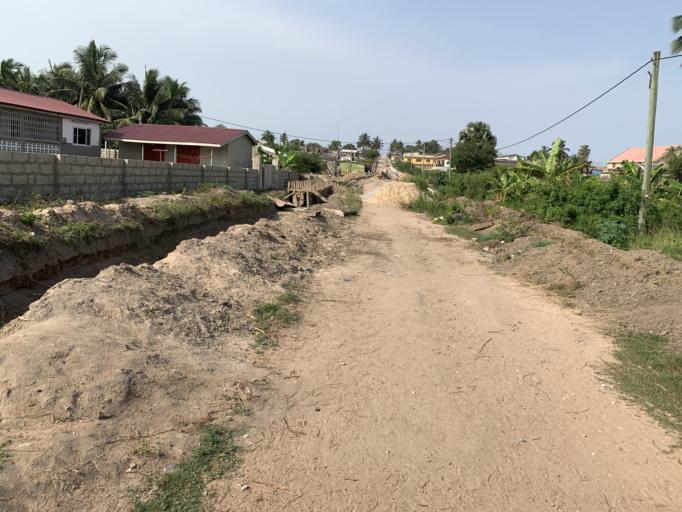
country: GH
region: Central
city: Winneba
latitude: 5.3330
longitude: -0.6254
